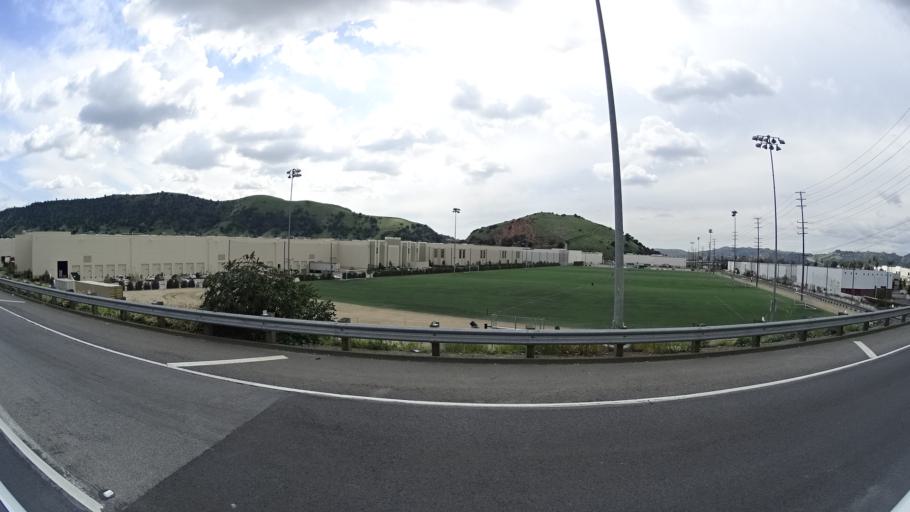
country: US
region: California
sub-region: Los Angeles County
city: Pomona
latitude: 34.0566
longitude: -117.7844
